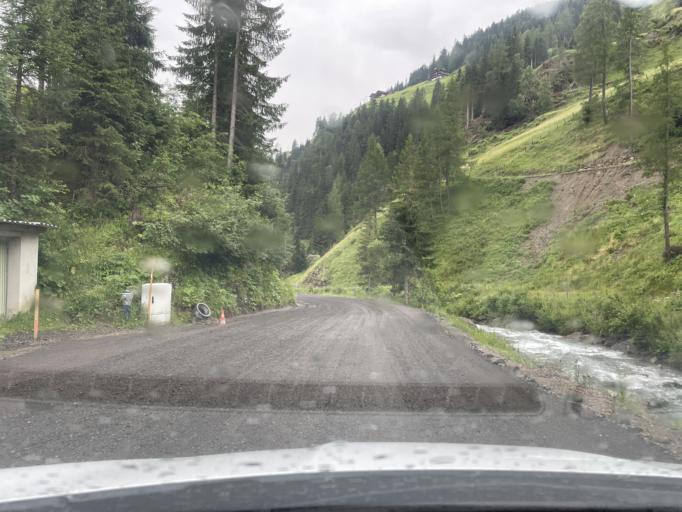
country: AT
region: Tyrol
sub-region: Politischer Bezirk Lienz
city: Ausservillgraten
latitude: 46.8003
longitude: 12.4502
